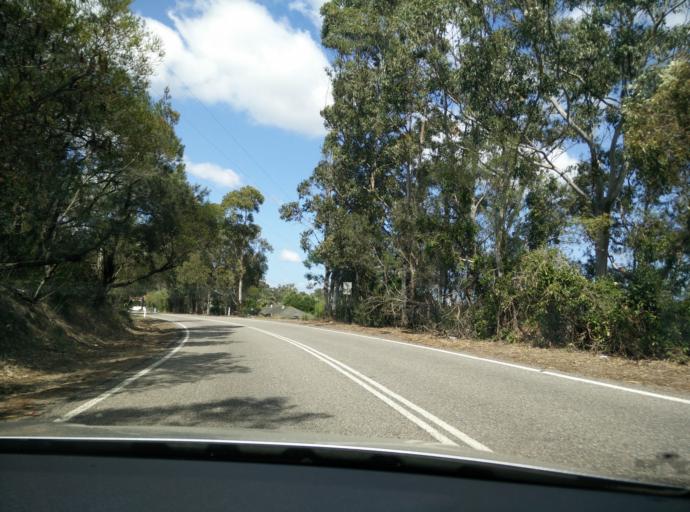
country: AU
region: New South Wales
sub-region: Gosford Shire
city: Point Clare
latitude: -33.4443
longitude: 151.2928
